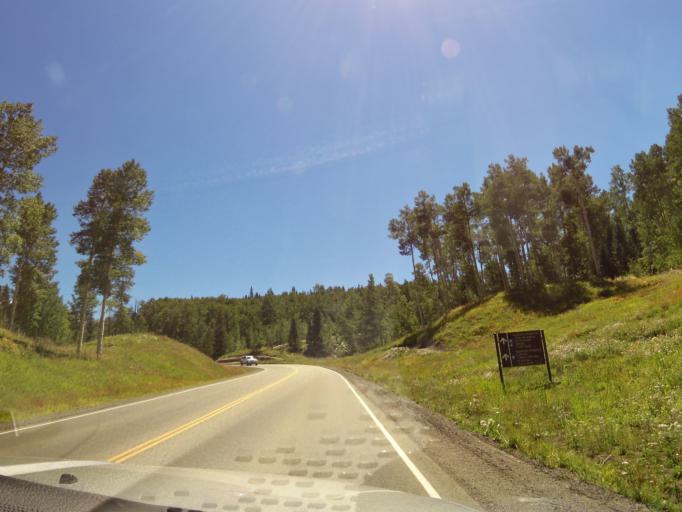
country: US
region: Colorado
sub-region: San Miguel County
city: Mountain Village
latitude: 37.9349
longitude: -107.8626
